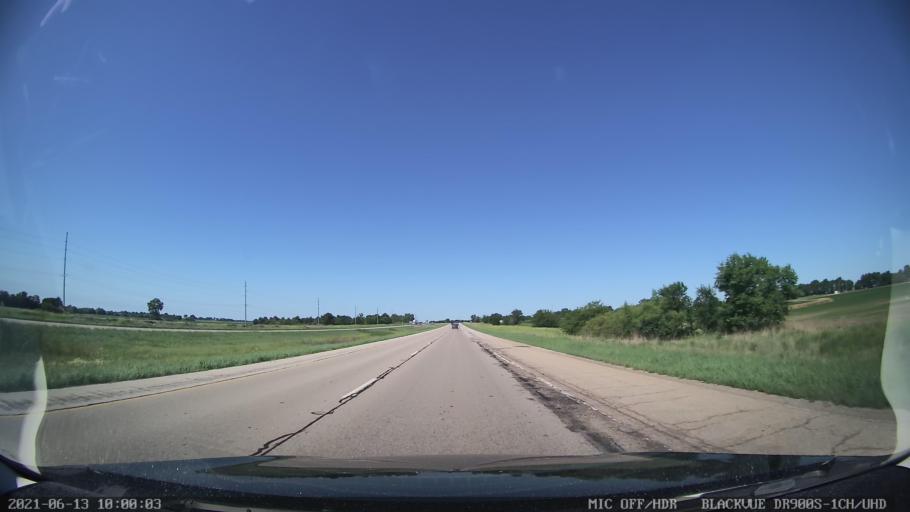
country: US
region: Illinois
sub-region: Logan County
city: Atlanta
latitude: 40.3085
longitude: -89.1697
